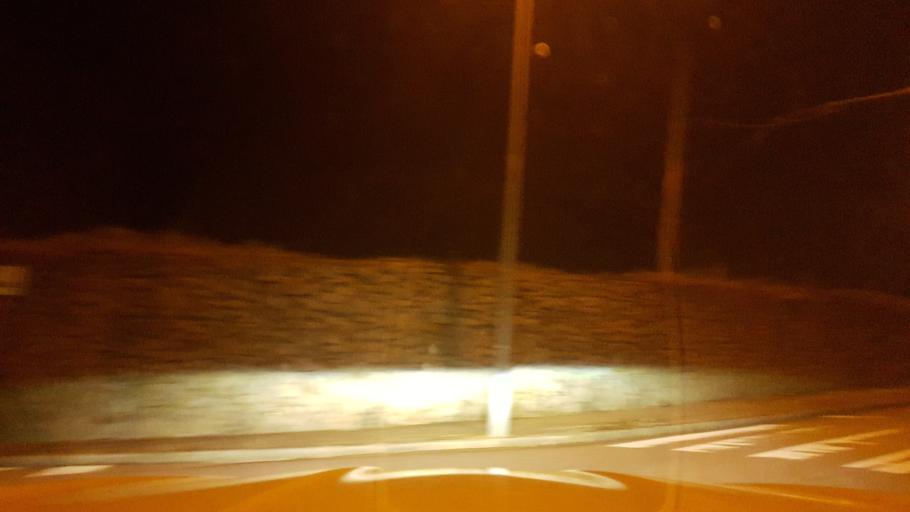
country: PT
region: Porto
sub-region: Matosinhos
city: Guifoes
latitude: 41.2163
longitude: -8.6461
